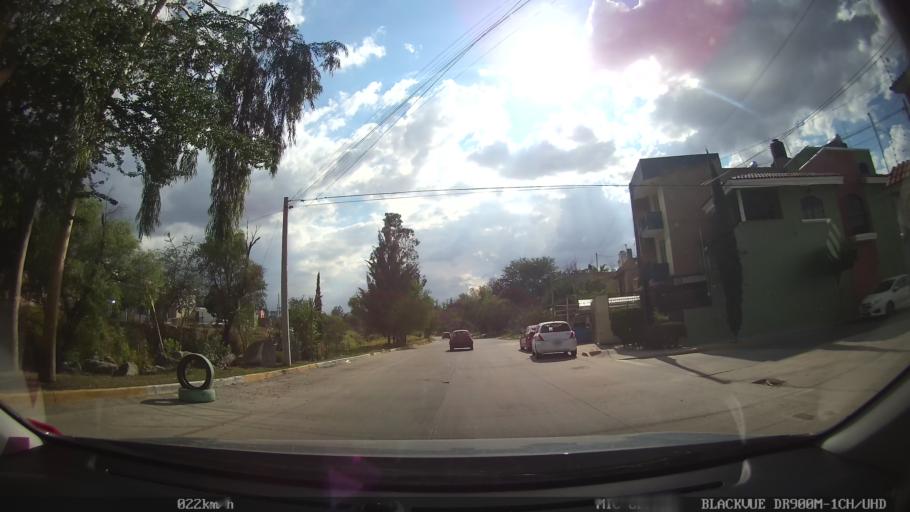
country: MX
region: Jalisco
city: Tlaquepaque
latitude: 20.6444
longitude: -103.2760
